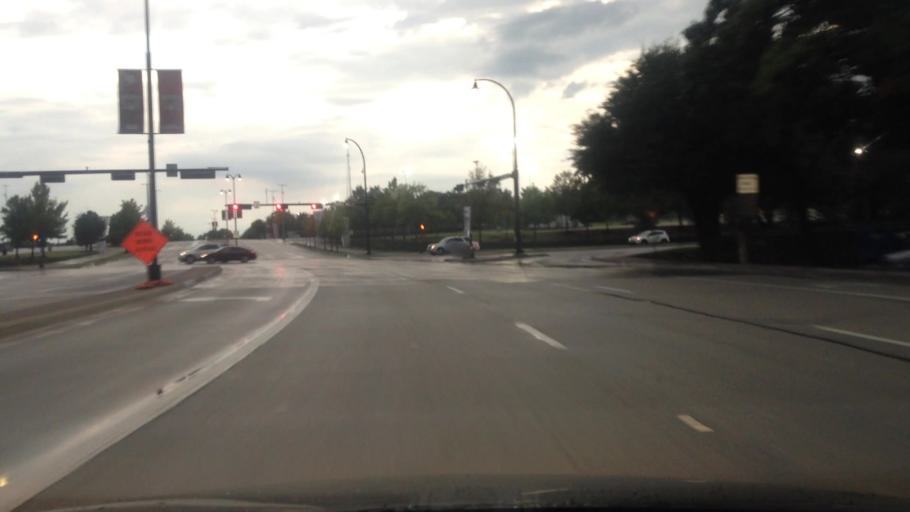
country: US
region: Texas
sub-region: Tarrant County
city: Arlington
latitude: 32.7512
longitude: -97.0895
